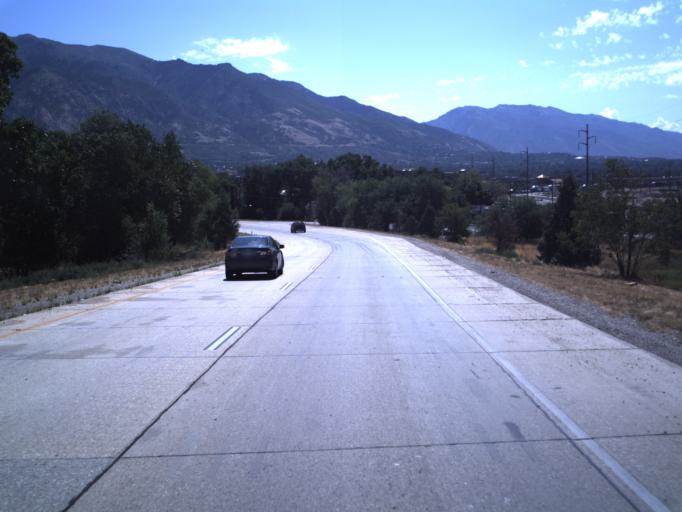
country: US
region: Utah
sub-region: Weber County
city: Ogden
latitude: 41.2305
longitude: -111.9857
